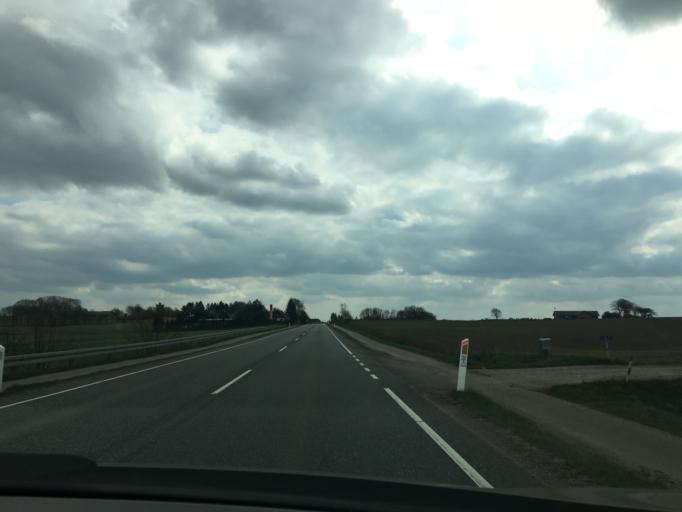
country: DK
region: Central Jutland
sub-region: Horsens Kommune
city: Braedstrup
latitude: 55.9912
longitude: 9.6044
